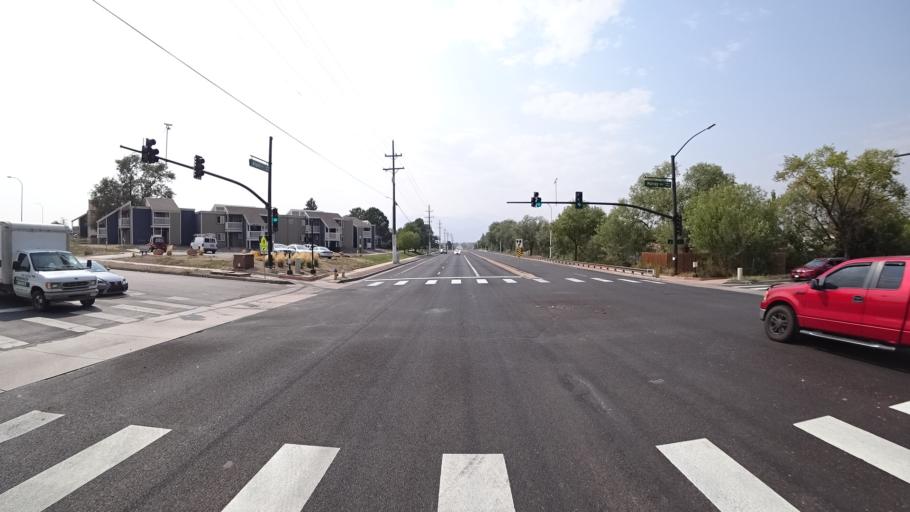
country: US
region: Colorado
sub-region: El Paso County
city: Cimarron Hills
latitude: 38.8253
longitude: -104.7485
